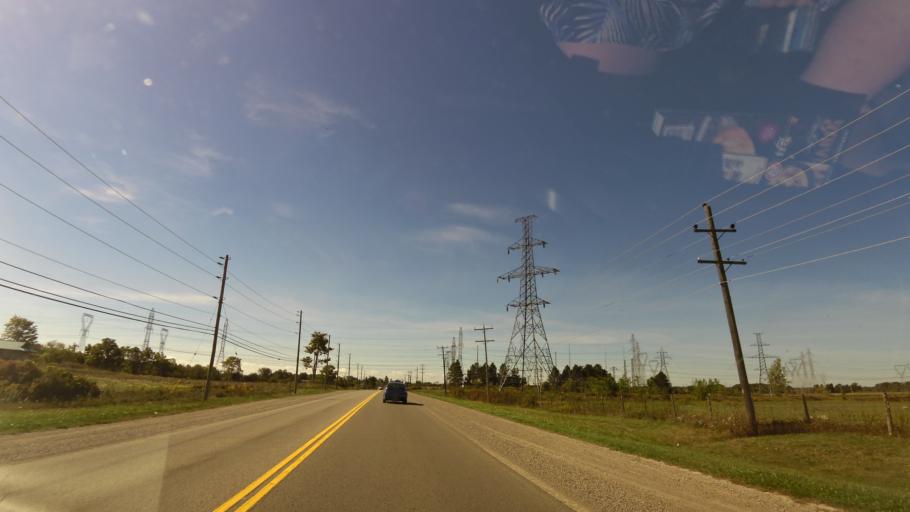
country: CA
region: Ontario
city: Ancaster
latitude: 43.0531
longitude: -79.9697
